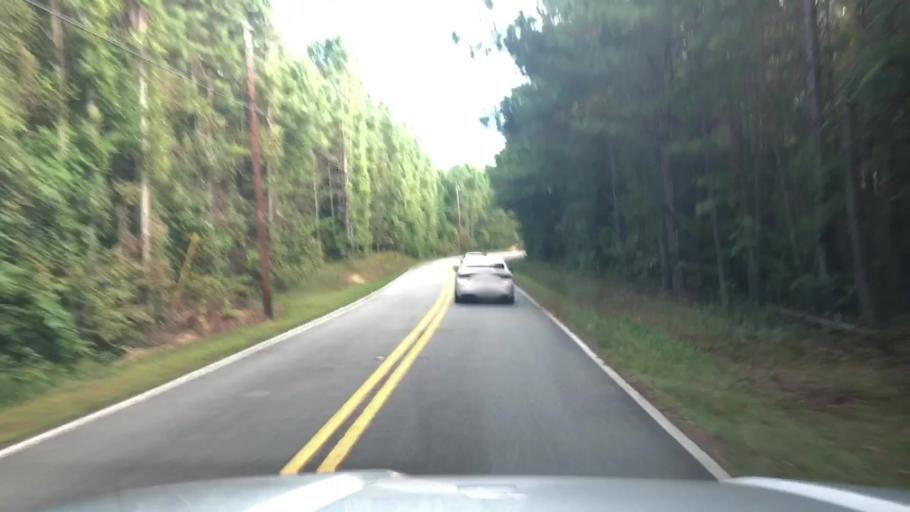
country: US
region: Georgia
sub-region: Bartow County
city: Euharlee
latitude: 34.0446
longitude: -84.8663
